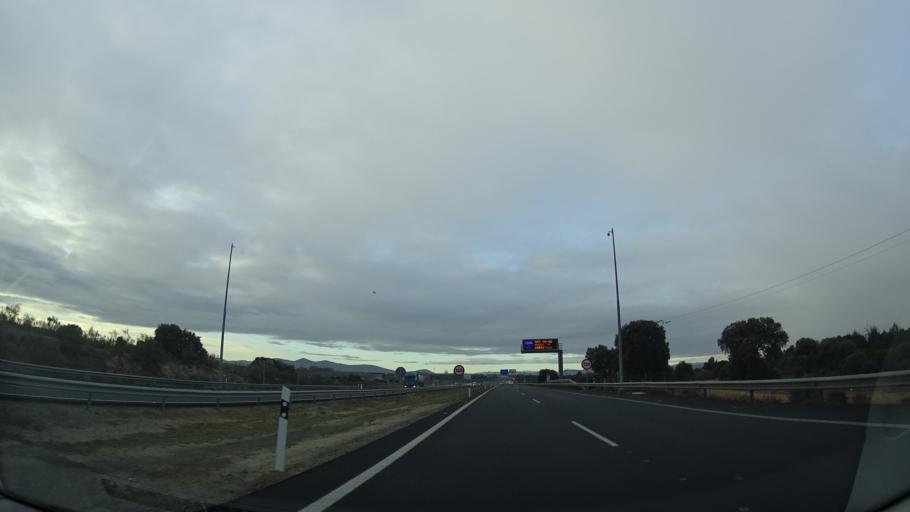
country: ES
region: Castille-La Mancha
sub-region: Province of Toledo
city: Burguillos de Toledo
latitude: 39.8287
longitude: -3.9809
